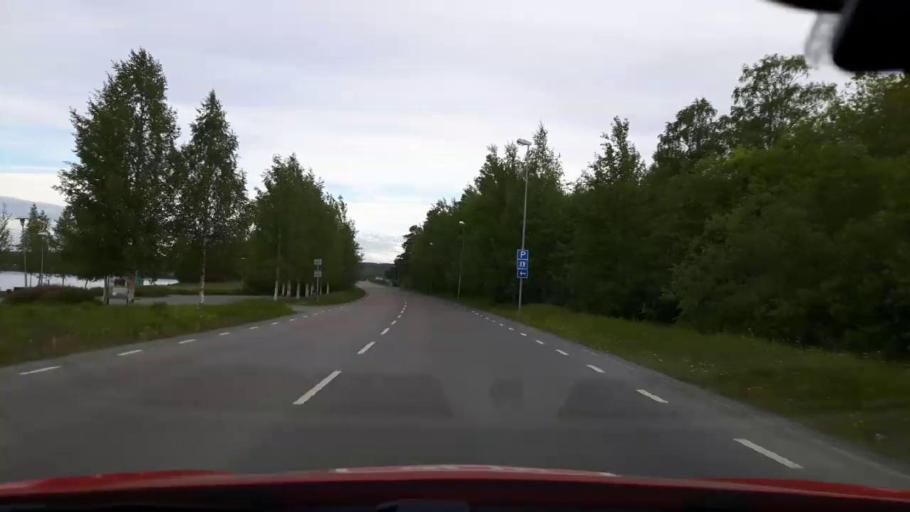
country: SE
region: Jaemtland
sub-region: OEstersunds Kommun
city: Ostersund
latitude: 63.1706
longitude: 14.6098
